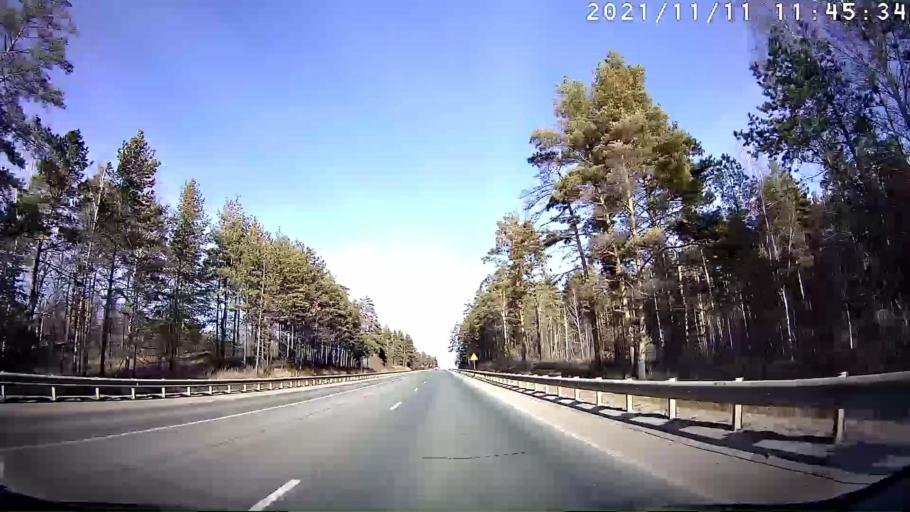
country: RU
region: Samara
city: Varlamovo
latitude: 53.4732
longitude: 48.3363
